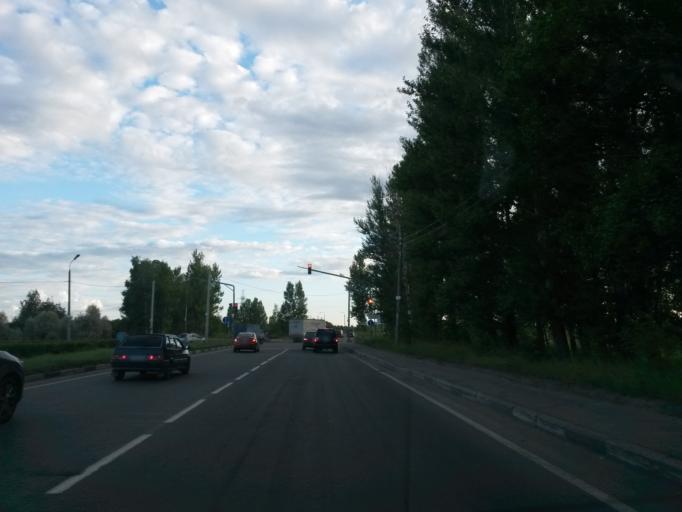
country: RU
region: Jaroslavl
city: Yaroslavl
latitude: 57.6724
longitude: 39.7713
